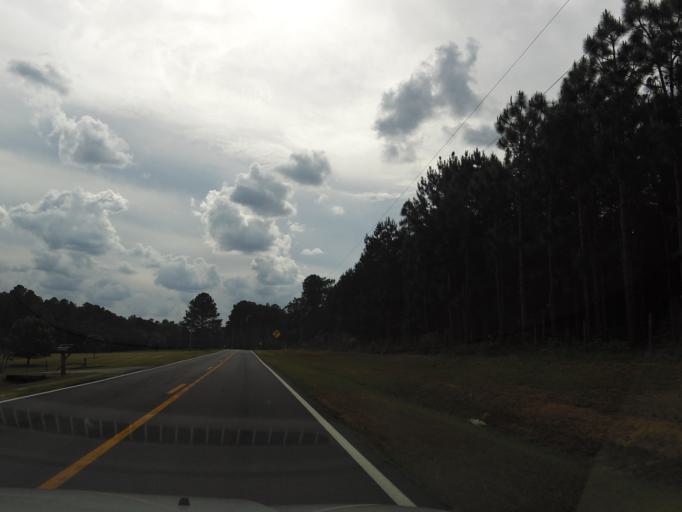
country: US
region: Georgia
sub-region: McDuffie County
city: Thomson
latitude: 33.5221
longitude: -82.4553
